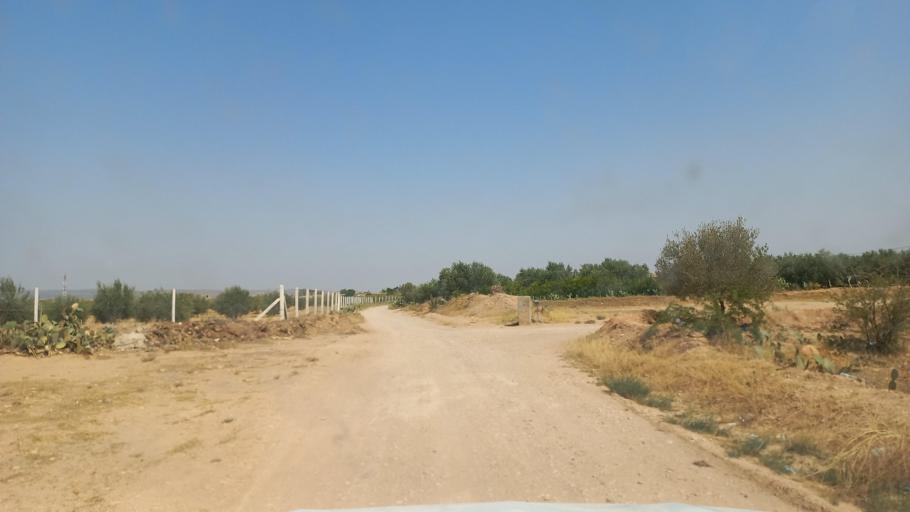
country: TN
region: Al Qasrayn
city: Kasserine
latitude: 35.2488
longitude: 9.0173
